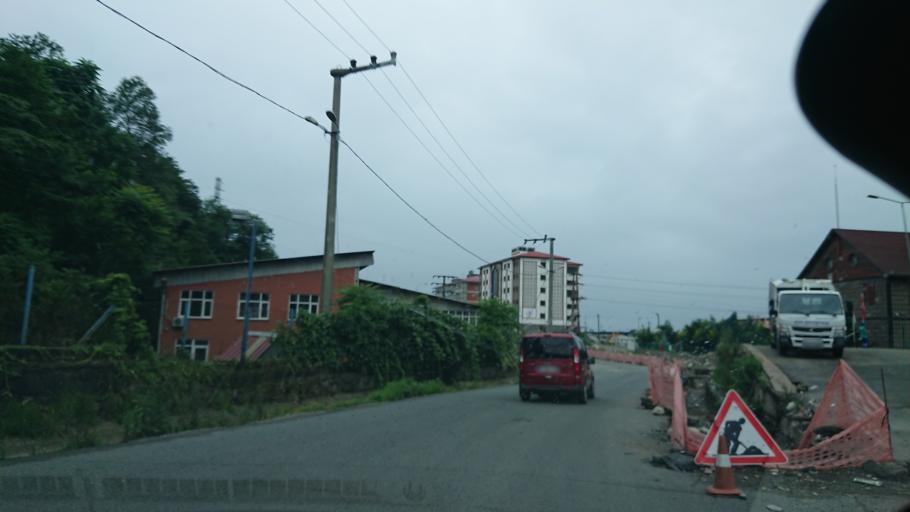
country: TR
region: Rize
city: Gundogdu
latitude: 41.0374
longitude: 40.5790
